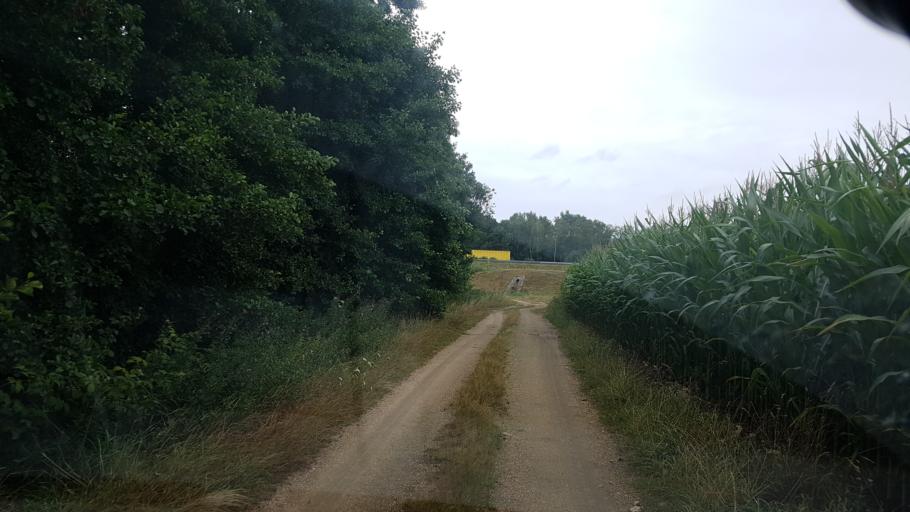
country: DE
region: Saxony
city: Reichenbach
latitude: 51.2111
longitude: 14.7921
